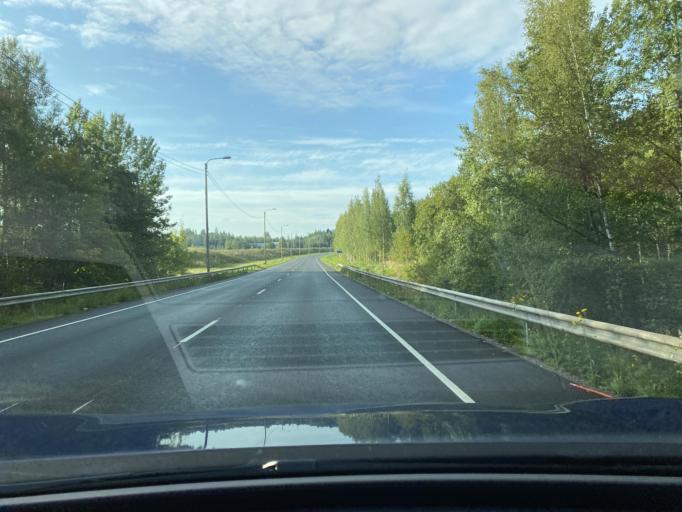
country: FI
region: Kymenlaakso
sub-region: Kouvola
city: Kouvola
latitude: 60.8905
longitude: 26.6045
